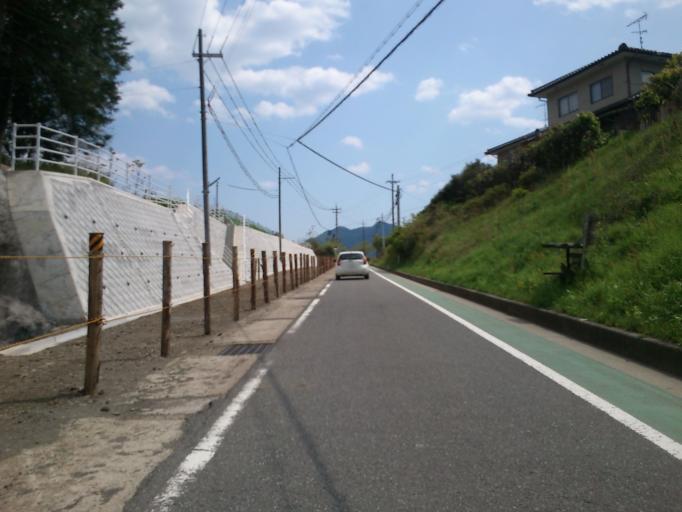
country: JP
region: Kyoto
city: Fukuchiyama
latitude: 35.3406
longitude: 134.9340
